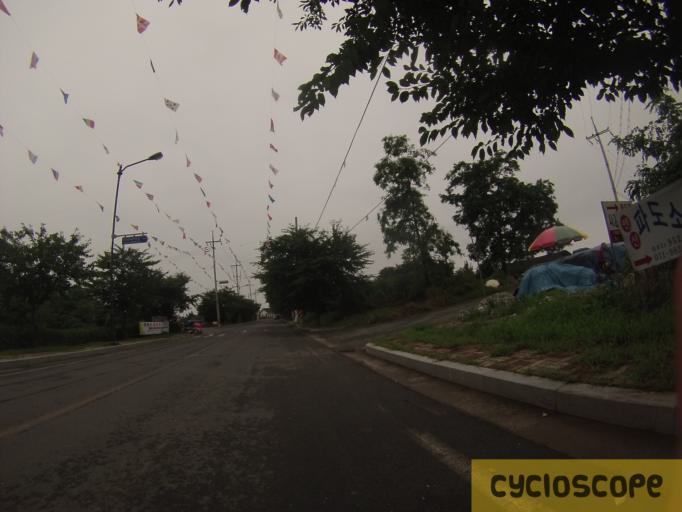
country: KR
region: Chungcheongnam-do
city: Taisen-ri
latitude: 36.2474
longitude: 126.5418
